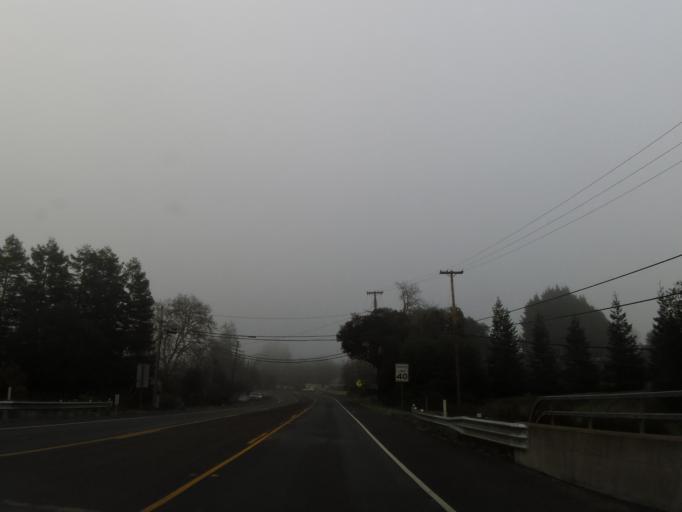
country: US
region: California
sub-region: Mendocino County
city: Boonville
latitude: 39.0140
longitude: -123.3728
